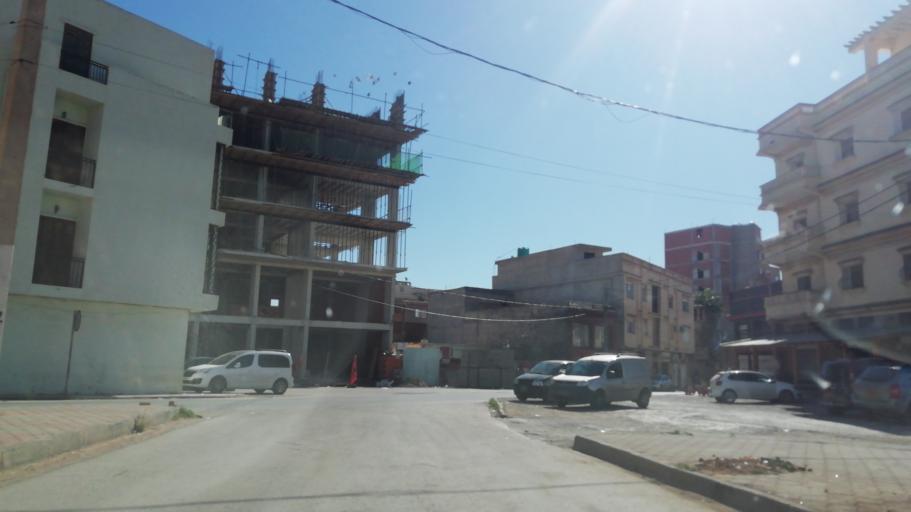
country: DZ
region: Oran
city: Oran
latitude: 35.6942
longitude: -0.6124
